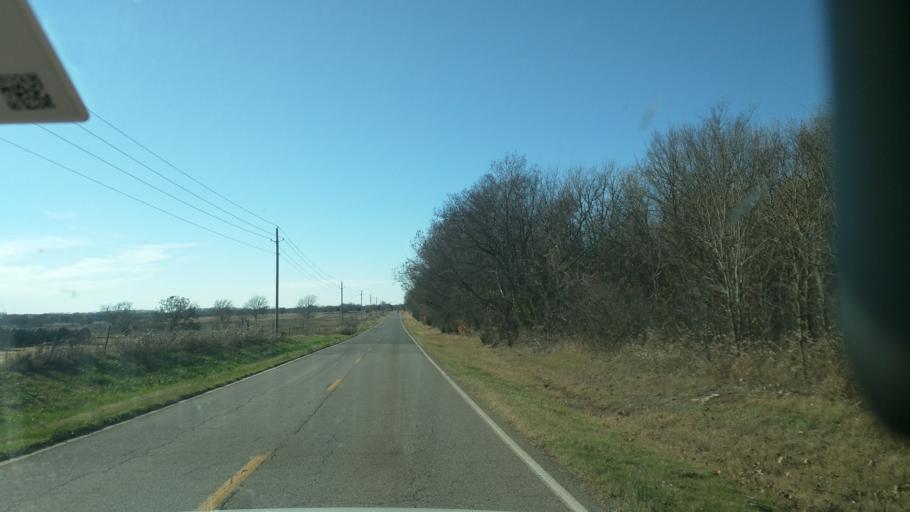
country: US
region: Oklahoma
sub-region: Nowata County
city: Nowata
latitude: 36.7716
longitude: -95.5813
